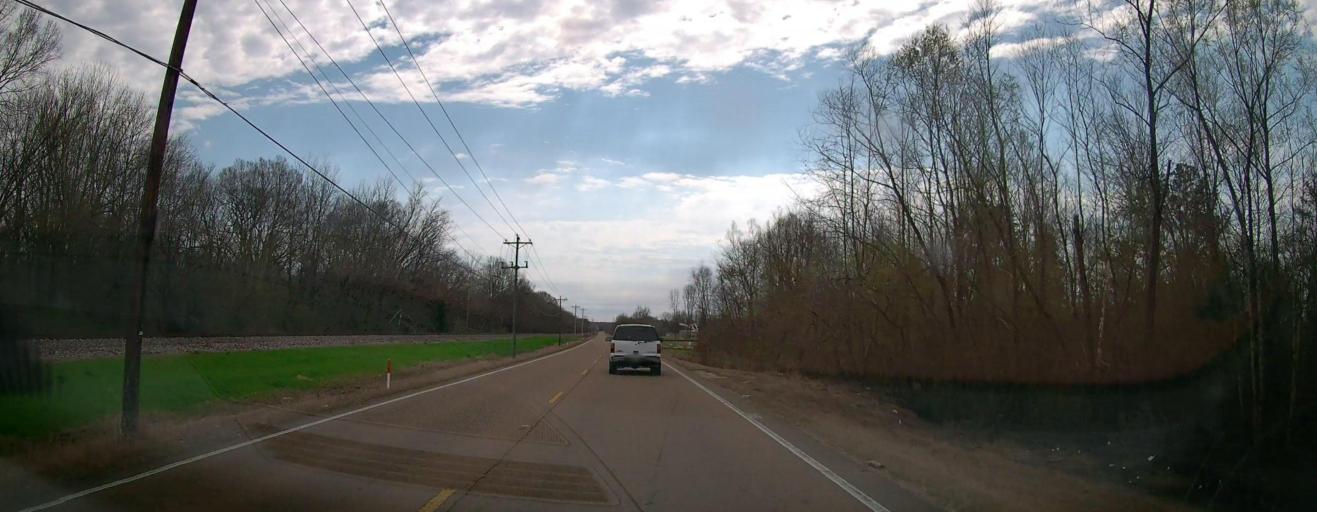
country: US
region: Mississippi
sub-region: De Soto County
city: Olive Branch
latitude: 34.9148
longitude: -89.7644
